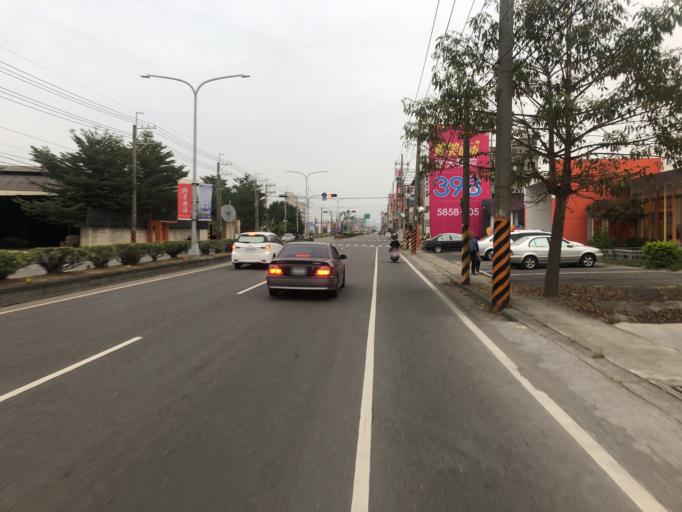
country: TW
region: Taiwan
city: Yujing
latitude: 23.1288
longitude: 120.3126
